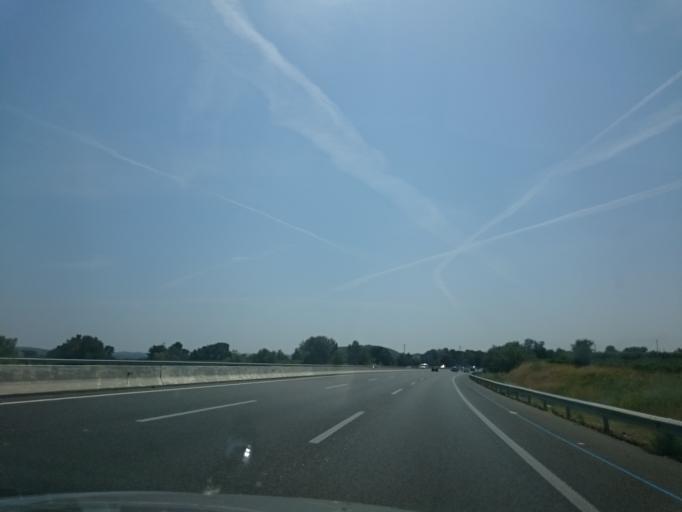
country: ES
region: Catalonia
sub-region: Provincia de Barcelona
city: Castellet
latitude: 41.3188
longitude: 1.6390
